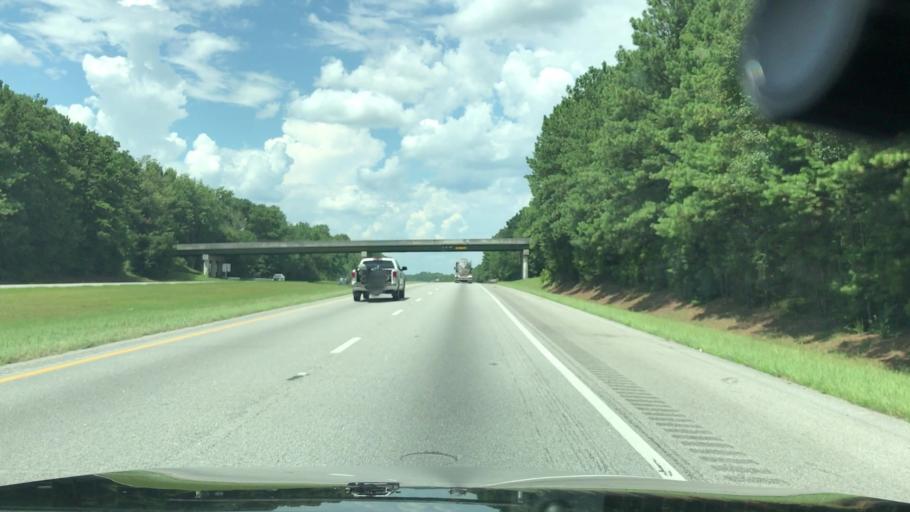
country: US
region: South Carolina
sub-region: Chester County
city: Eureka Mill
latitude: 34.6951
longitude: -81.0295
